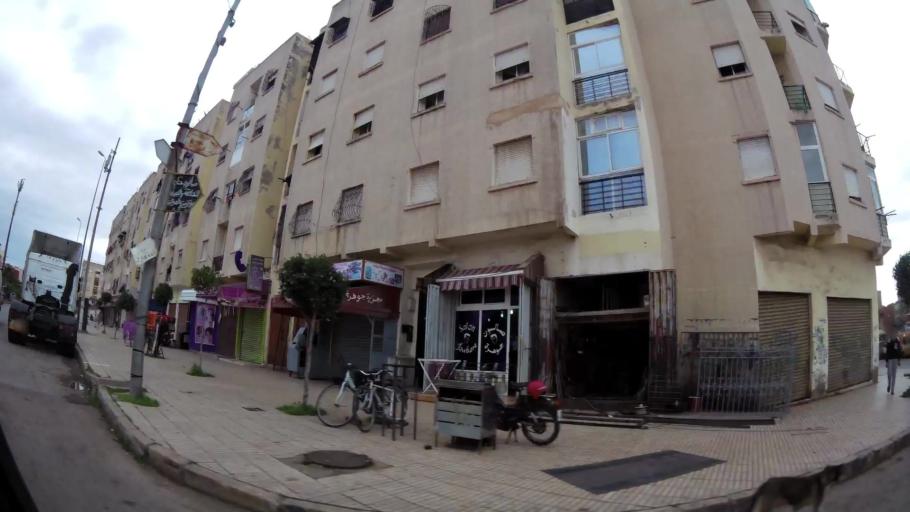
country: MA
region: Grand Casablanca
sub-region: Mediouna
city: Tit Mellil
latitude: 33.5582
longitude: -7.5331
